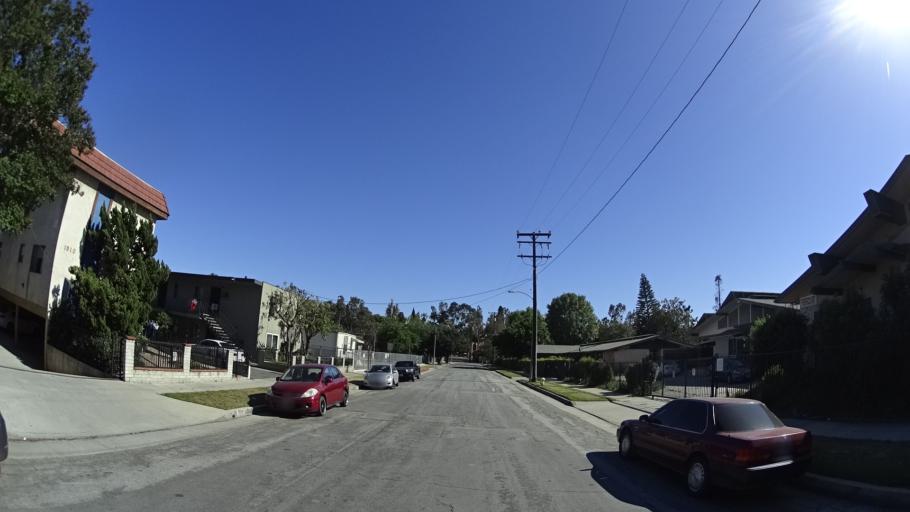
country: US
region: California
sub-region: Los Angeles County
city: Monterey Park
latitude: 34.0762
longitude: -118.1400
